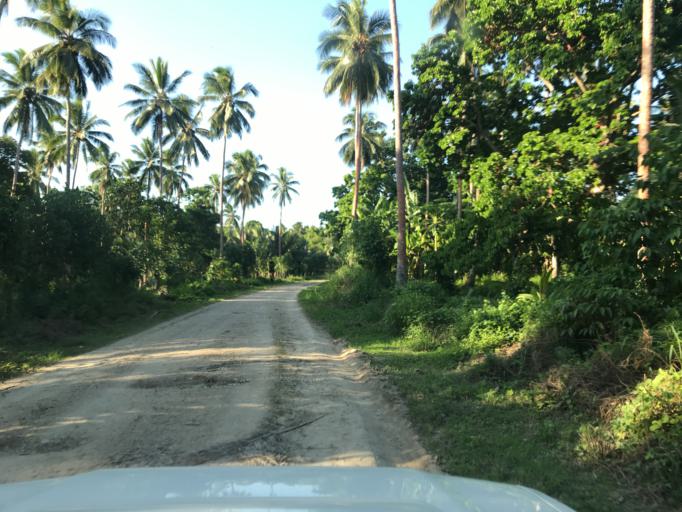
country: VU
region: Sanma
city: Luganville
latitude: -15.5917
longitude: 166.8984
